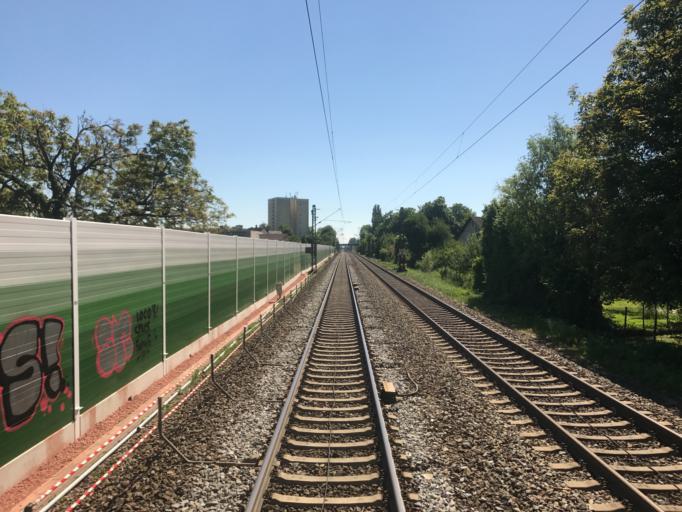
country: DE
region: Baden-Wuerttemberg
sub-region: Freiburg Region
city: Lahr
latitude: 48.3483
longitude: 7.8407
